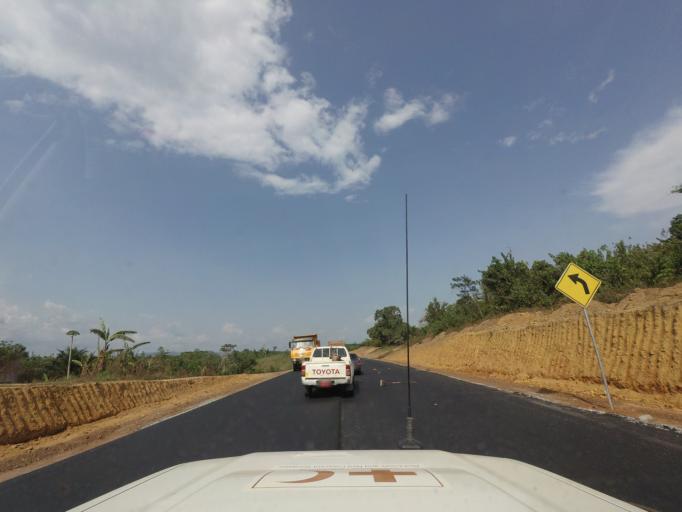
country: LR
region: Margibi
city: Kakata
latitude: 6.7338
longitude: -10.1269
